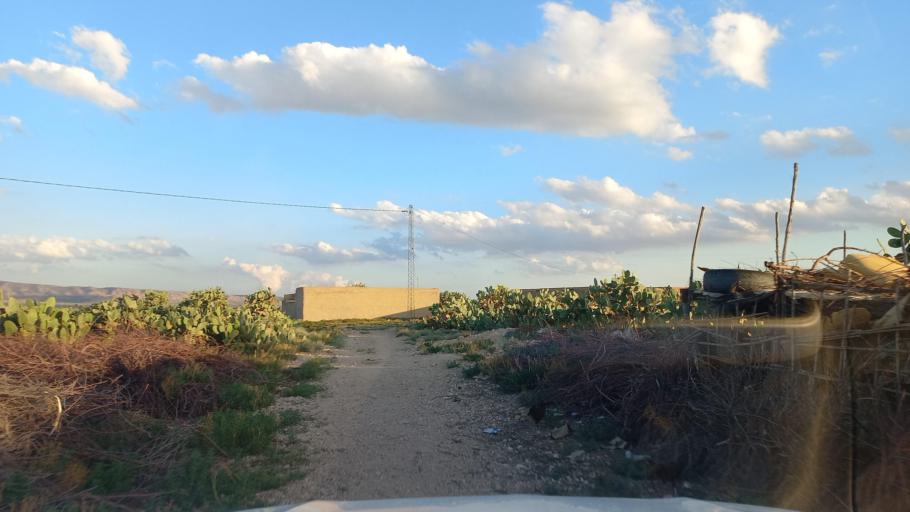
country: TN
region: Al Qasrayn
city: Sbiba
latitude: 35.3764
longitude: 9.0490
